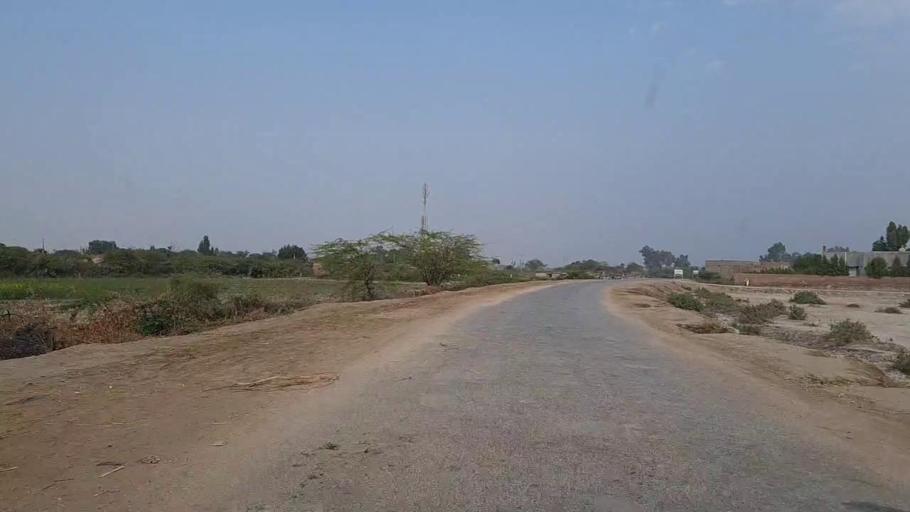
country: PK
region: Sindh
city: Mirwah Gorchani
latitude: 25.4249
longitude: 69.1515
